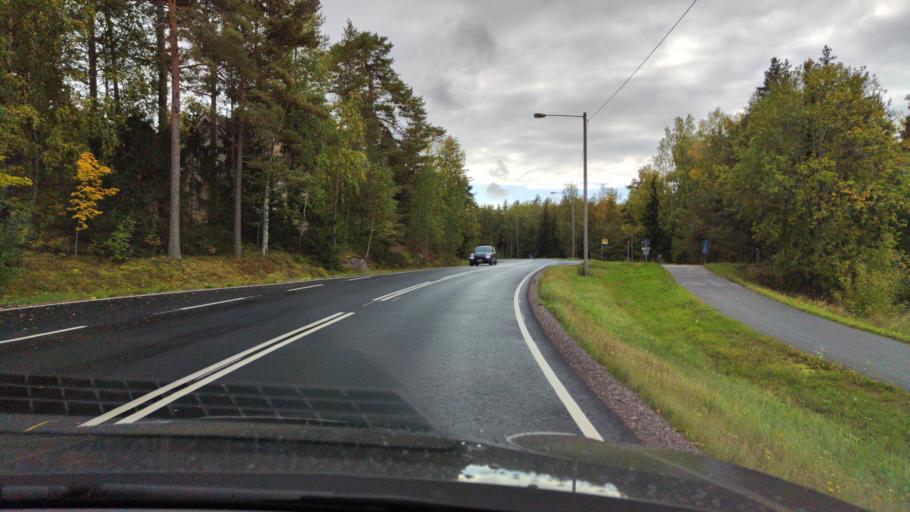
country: FI
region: Varsinais-Suomi
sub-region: Turku
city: Raisio
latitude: 60.3723
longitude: 22.1779
